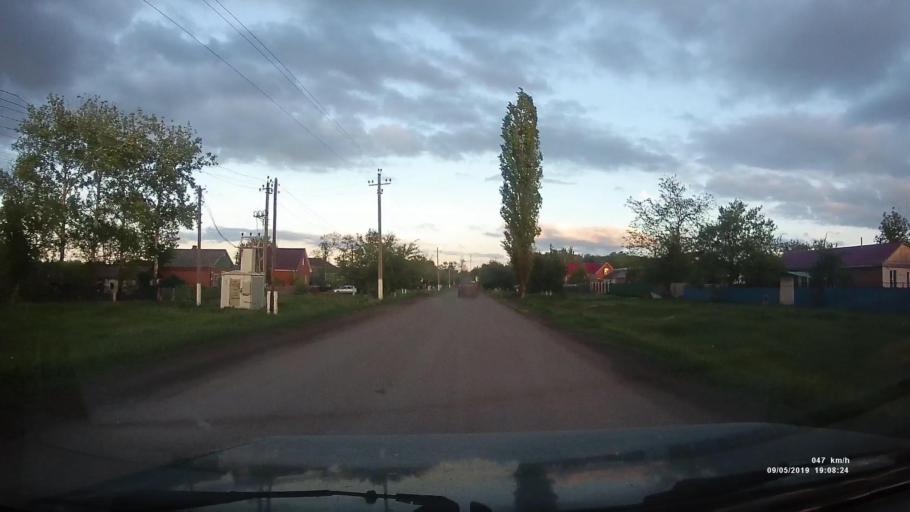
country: RU
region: Krasnodarskiy
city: Kanelovskaya
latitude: 46.7297
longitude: 39.2037
